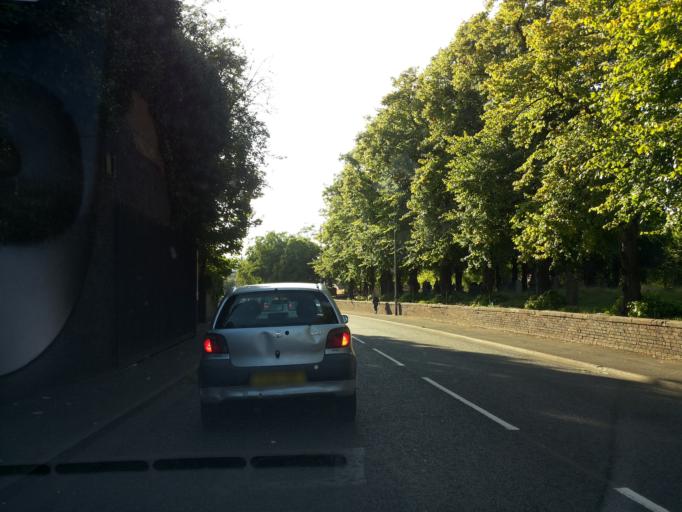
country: GB
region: England
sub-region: Worcestershire
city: Kidderminster
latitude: 52.3900
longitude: -2.2417
